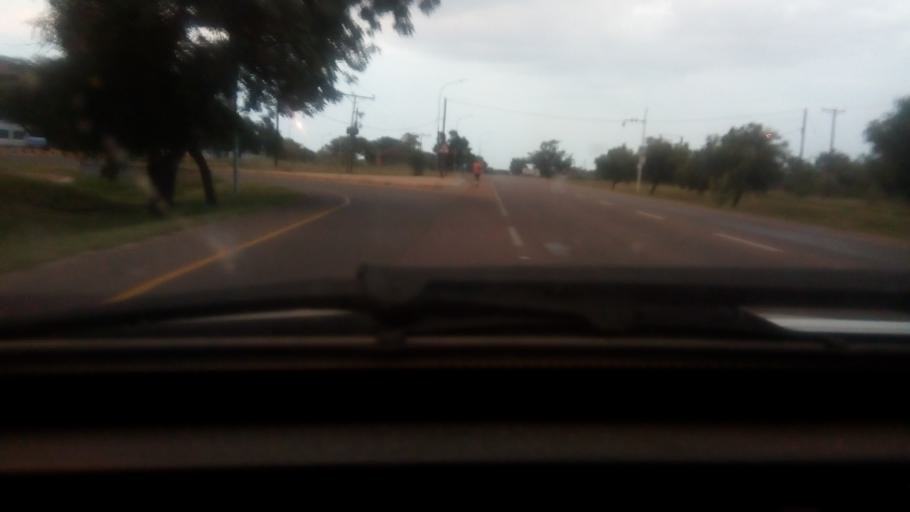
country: BW
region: Kweneng
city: Mmopone
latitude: -24.5881
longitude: 25.9170
